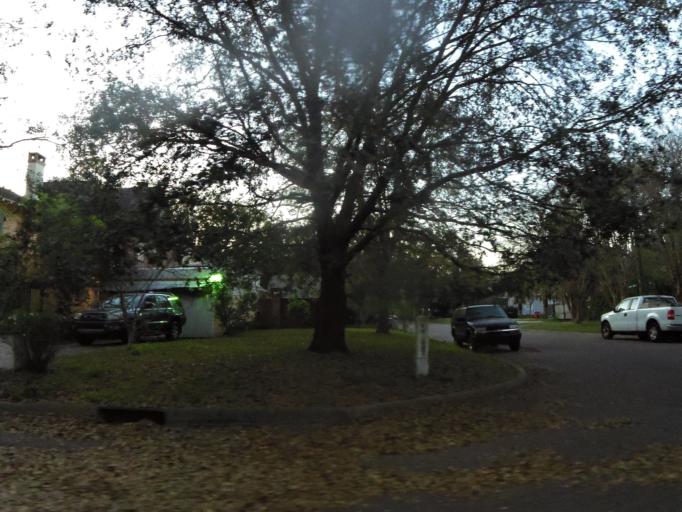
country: US
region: Florida
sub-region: Duval County
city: Jacksonville
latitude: 30.3035
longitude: -81.7066
